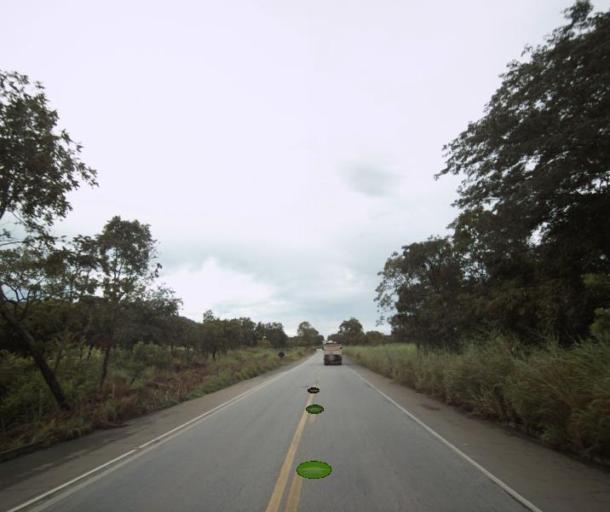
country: BR
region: Goias
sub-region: Porangatu
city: Porangatu
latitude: -13.6298
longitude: -49.0424
